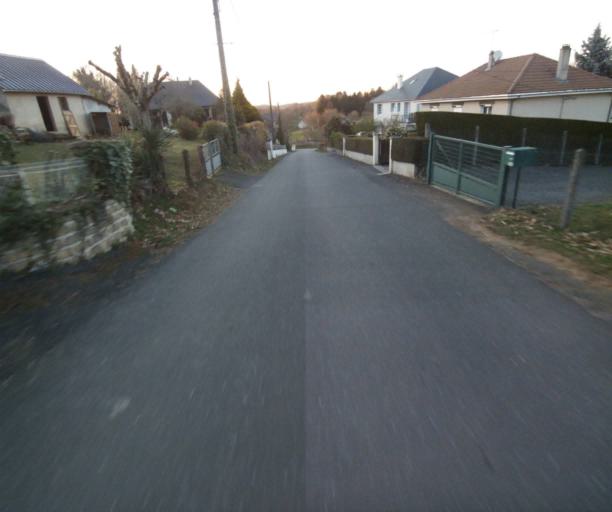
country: FR
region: Limousin
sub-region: Departement de la Correze
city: Saint-Clement
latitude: 45.3537
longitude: 1.6345
